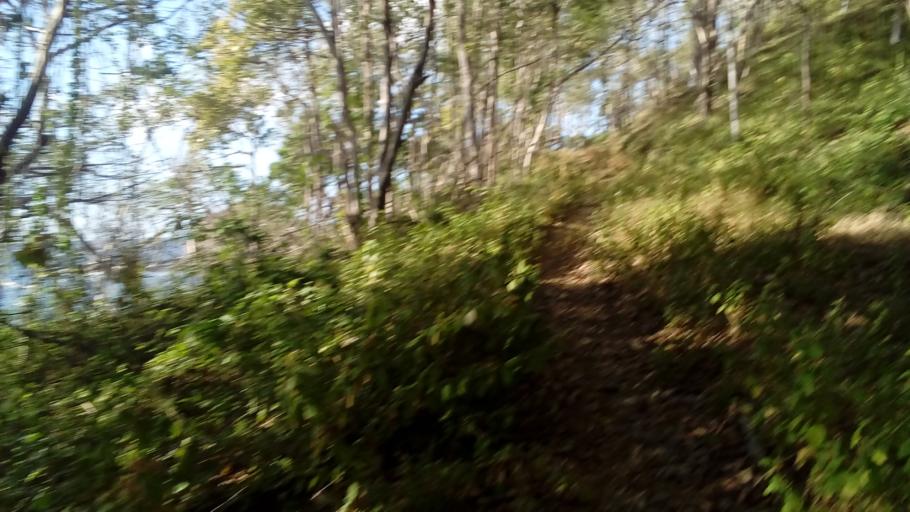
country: CR
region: Guanacaste
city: Sardinal
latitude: 10.3960
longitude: -85.8342
